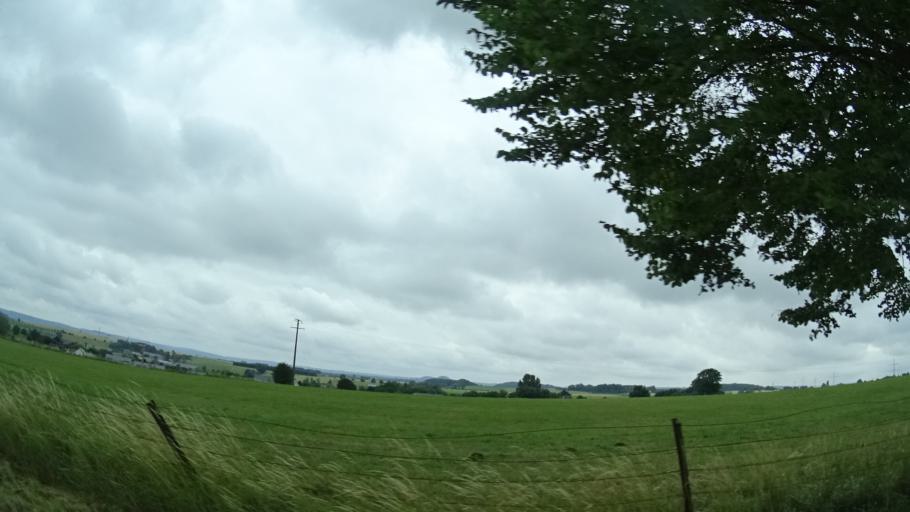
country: LU
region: Luxembourg
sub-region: Canton de Capellen
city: Dippach
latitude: 49.5792
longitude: 5.9867
